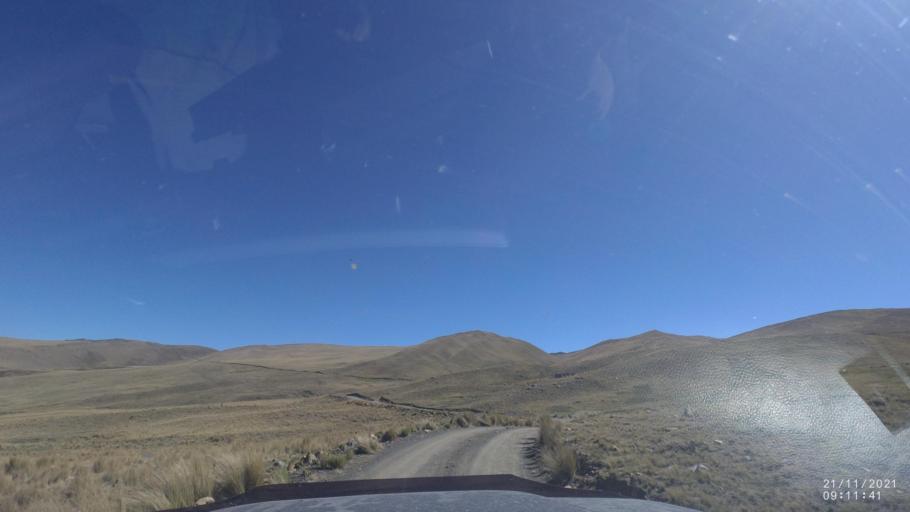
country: BO
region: Cochabamba
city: Cochabamba
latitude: -17.1459
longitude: -66.2579
